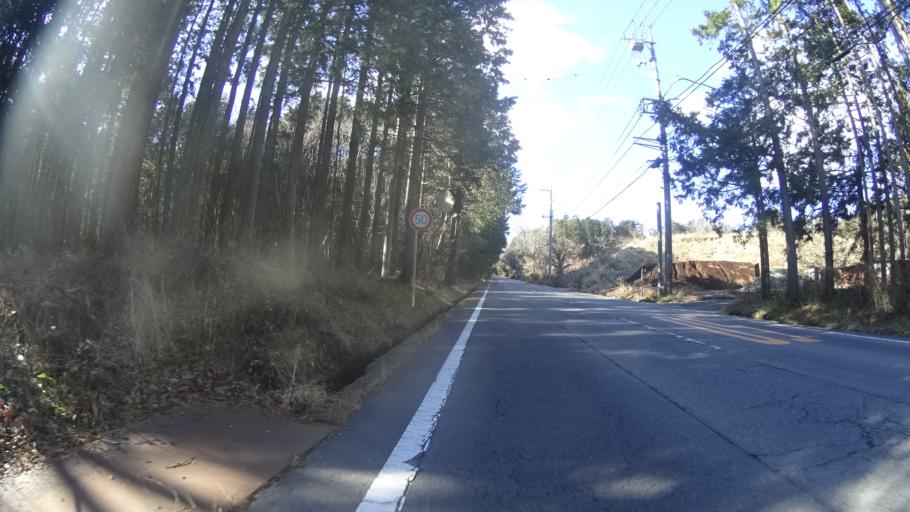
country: JP
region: Shizuoka
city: Gotemba
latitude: 35.3425
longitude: 138.9048
